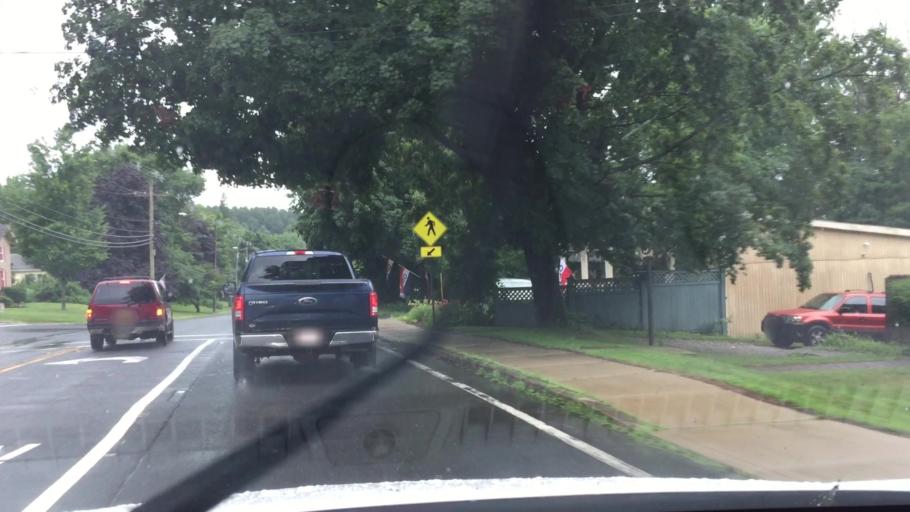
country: US
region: Massachusetts
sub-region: Berkshire County
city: Lanesborough
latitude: 42.5177
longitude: -73.2279
